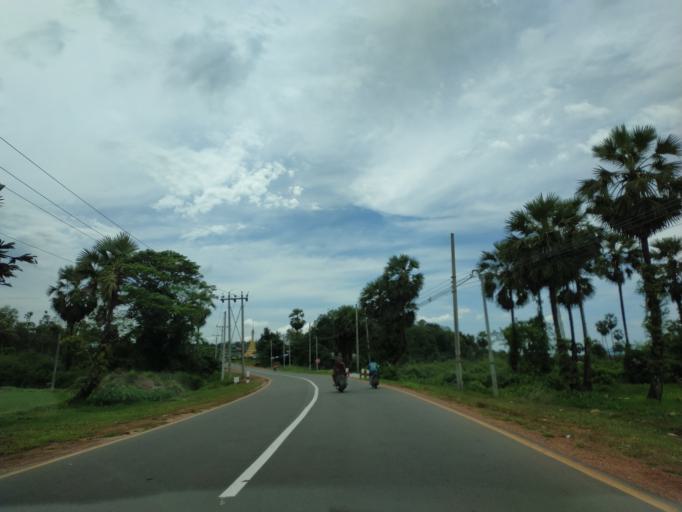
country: MM
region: Tanintharyi
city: Dawei
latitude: 14.0534
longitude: 98.2229
